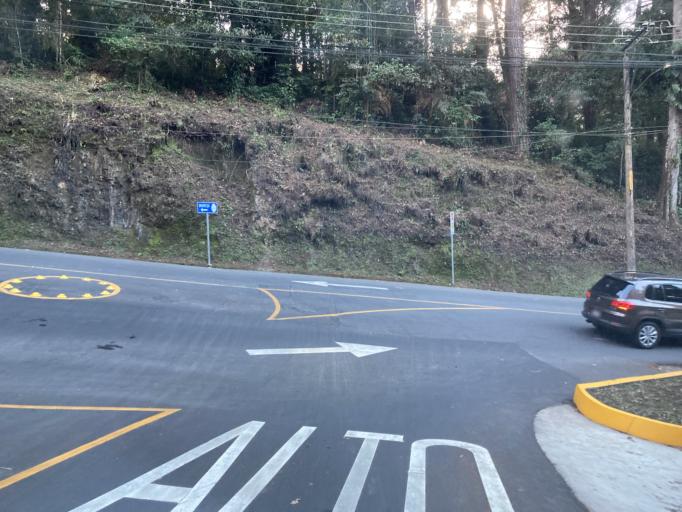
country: GT
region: Guatemala
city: Santa Catarina Pinula
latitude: 14.5562
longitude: -90.4643
